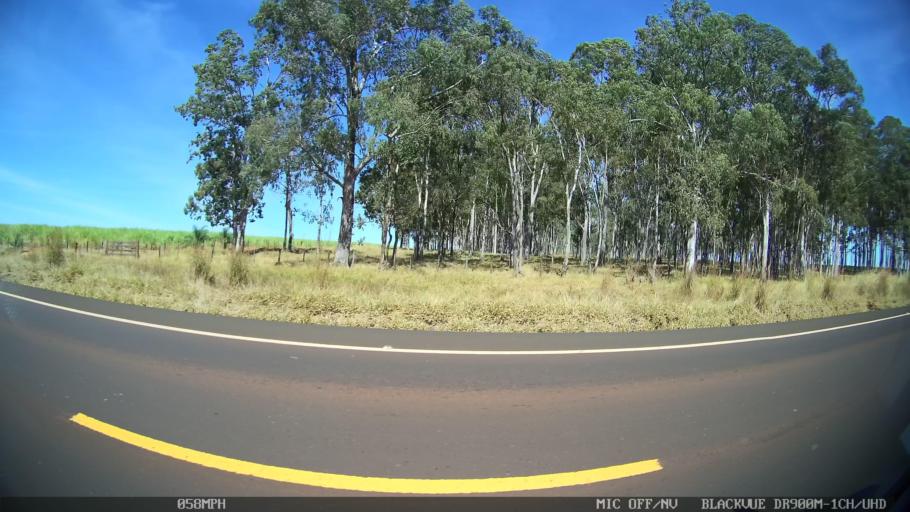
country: BR
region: Sao Paulo
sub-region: Franca
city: Franca
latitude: -20.5619
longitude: -47.5104
